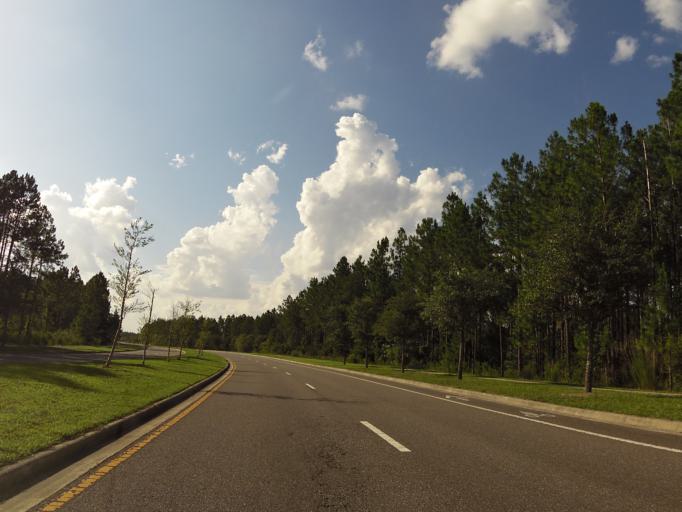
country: US
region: Florida
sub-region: Clay County
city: Green Cove Springs
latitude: 30.0349
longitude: -81.6133
